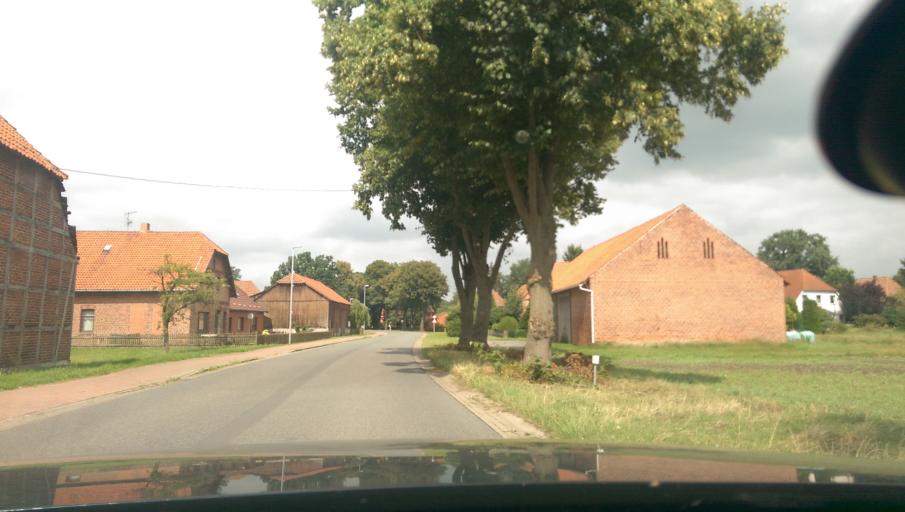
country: DE
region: Lower Saxony
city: Frankenfeld
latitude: 52.6918
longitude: 9.4812
